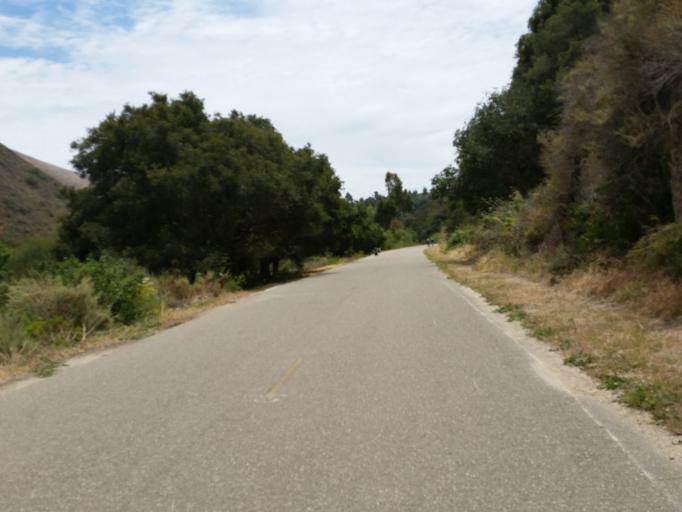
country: US
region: California
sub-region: San Luis Obispo County
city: Avila Beach
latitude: 35.1864
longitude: -120.7261
